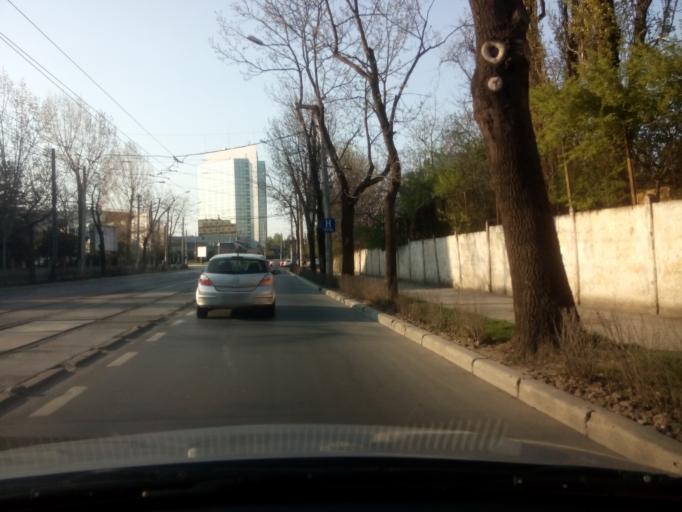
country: RO
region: Bucuresti
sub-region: Municipiul Bucuresti
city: Bucuresti
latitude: 44.4737
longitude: 26.0715
